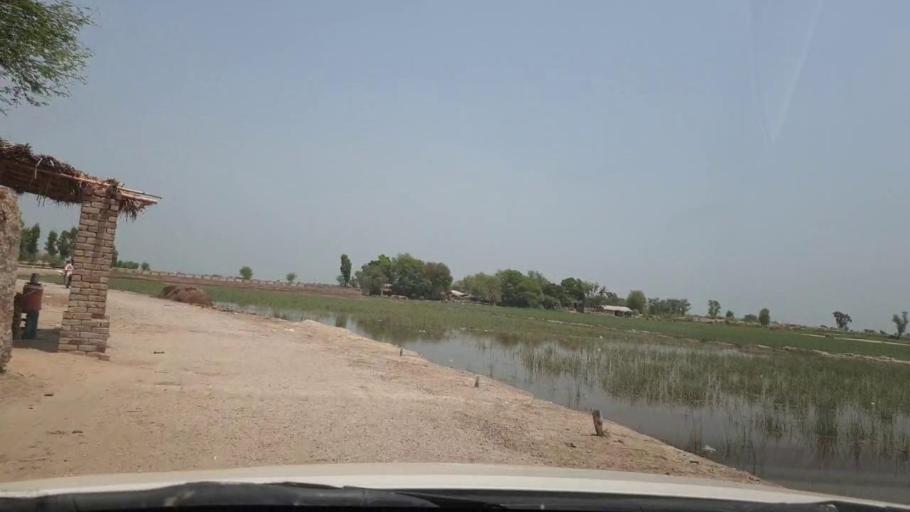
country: PK
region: Sindh
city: Rustam jo Goth
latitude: 28.0282
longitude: 68.7896
